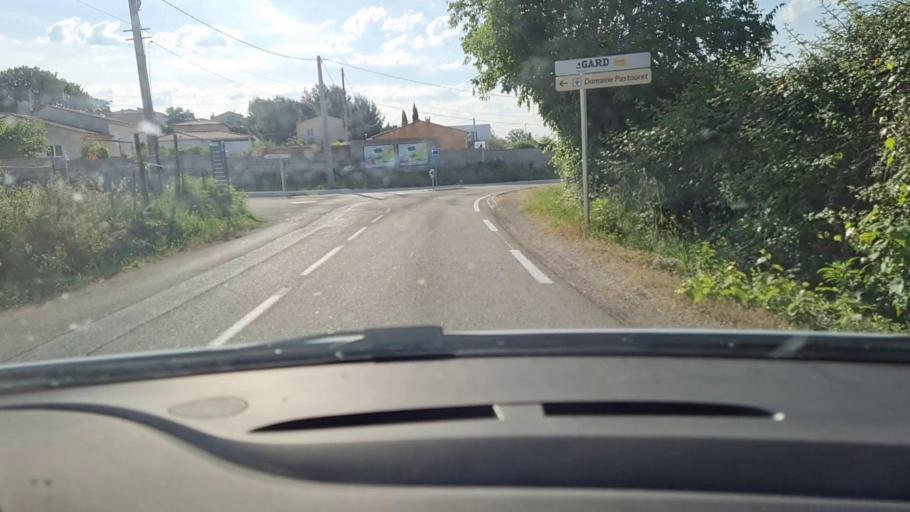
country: FR
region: Languedoc-Roussillon
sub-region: Departement du Gard
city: Bellegarde
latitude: 43.7599
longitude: 4.5102
